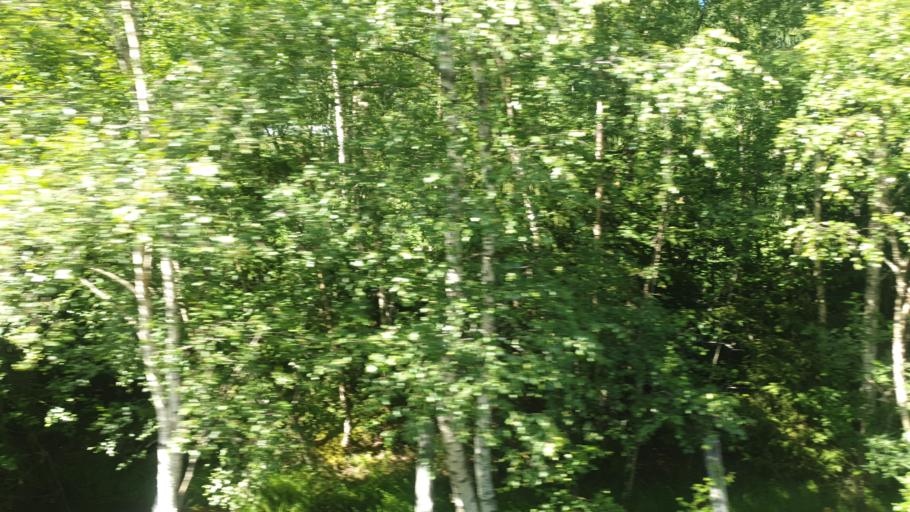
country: NO
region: Sor-Trondelag
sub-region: Meldal
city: Meldal
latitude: 63.1317
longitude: 9.7086
